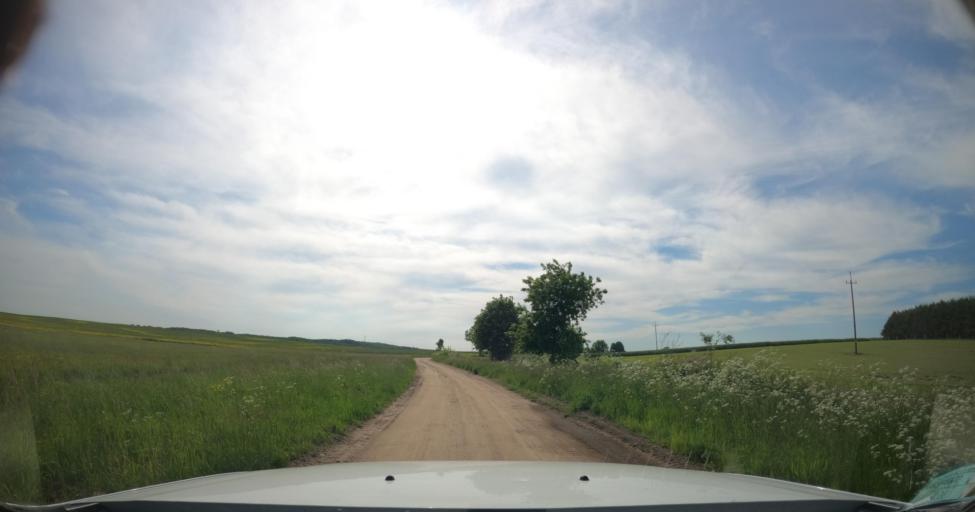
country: PL
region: Warmian-Masurian Voivodeship
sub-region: Powiat ostrodzki
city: Milakowo
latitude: 54.0154
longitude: 20.0145
